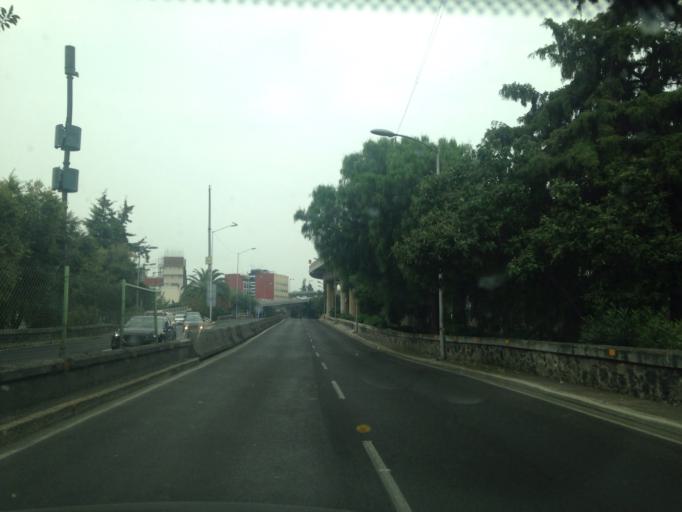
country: MX
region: Mexico City
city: Colonia del Valle
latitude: 19.3885
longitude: -99.1814
